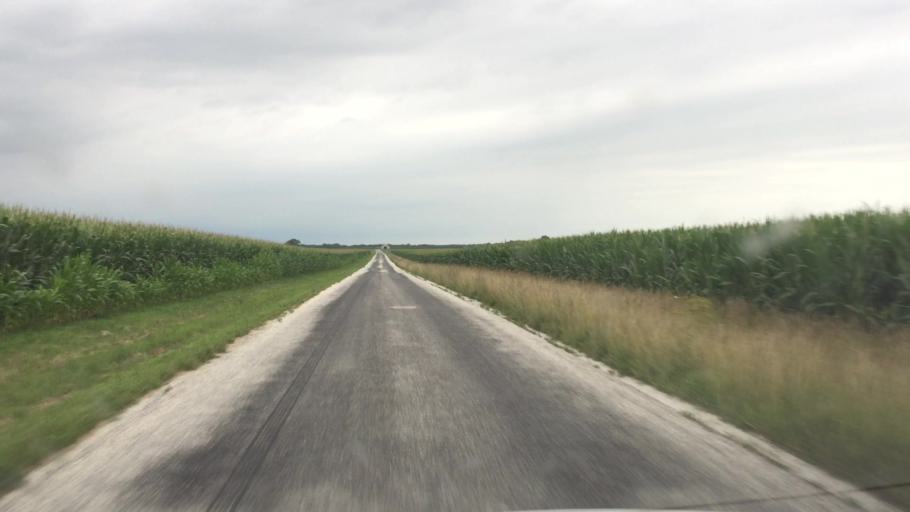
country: US
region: Illinois
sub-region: Adams County
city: Camp Point
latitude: 40.2178
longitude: -90.9692
